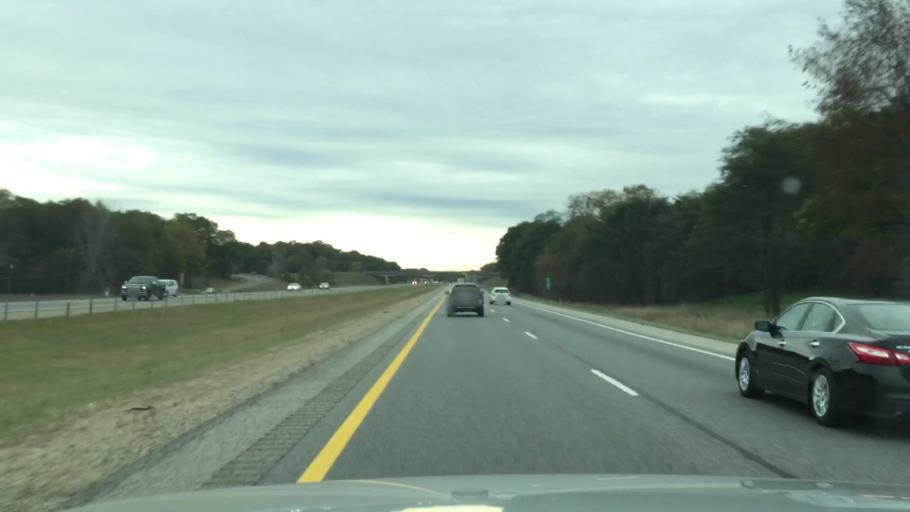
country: US
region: Michigan
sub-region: Van Buren County
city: Mattawan
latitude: 42.2299
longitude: -85.7208
